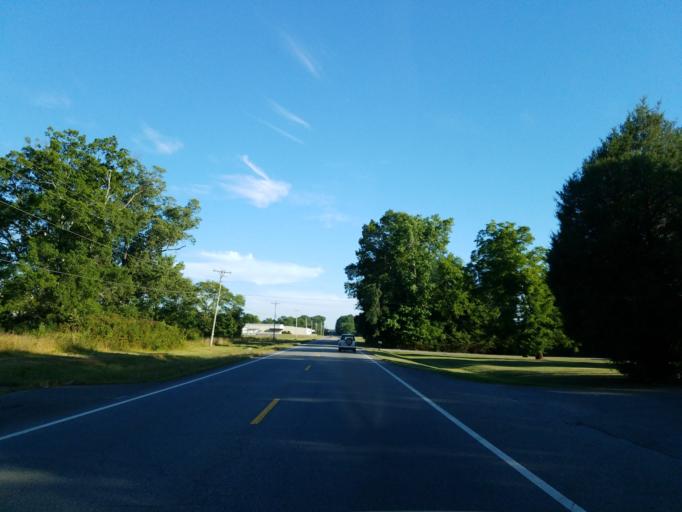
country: US
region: Georgia
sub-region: Gordon County
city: Calhoun
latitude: 34.4413
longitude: -84.9357
